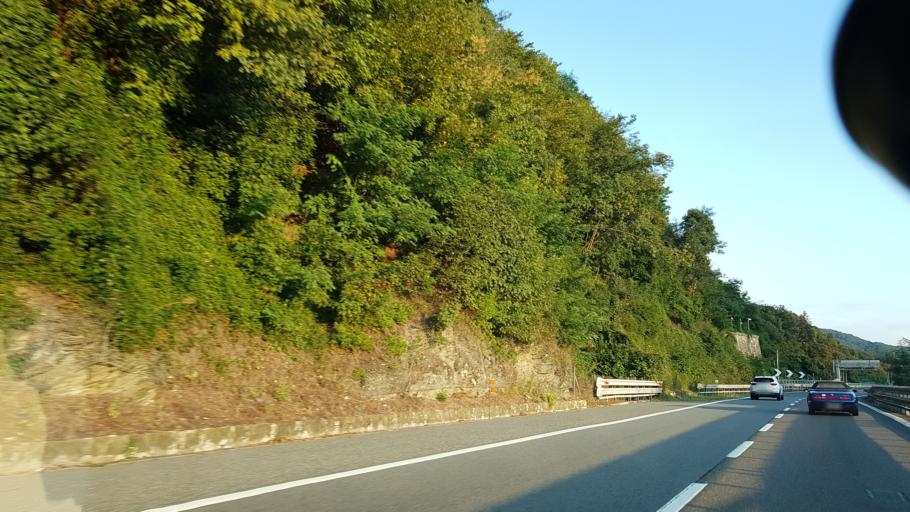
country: IT
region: Liguria
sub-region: Provincia di Genova
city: Borgo Fornari-Pieve
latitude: 44.5864
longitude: 8.9414
